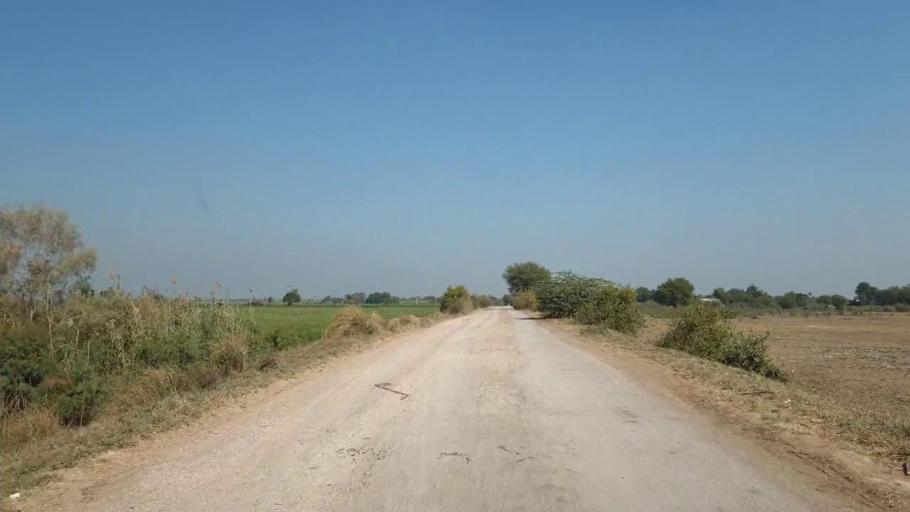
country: PK
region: Sindh
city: Shahdadpur
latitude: 25.9213
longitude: 68.5073
